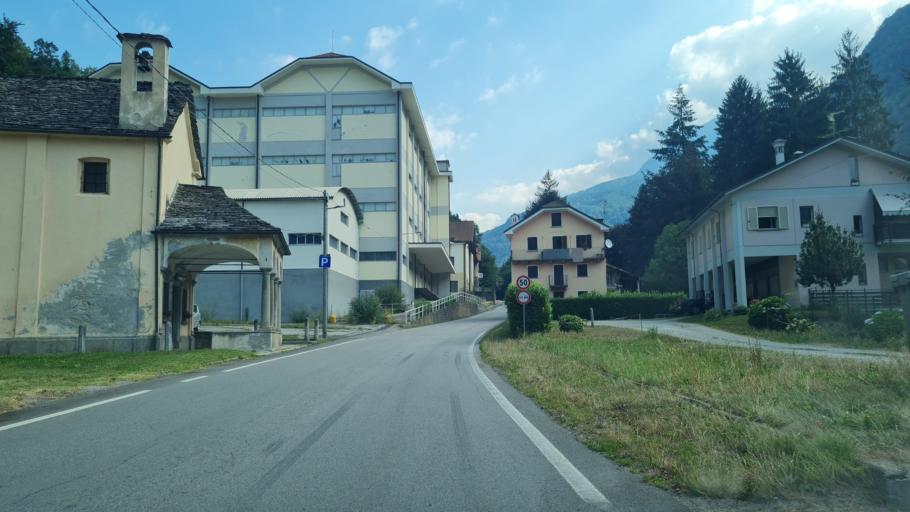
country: IT
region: Piedmont
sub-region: Provincia Verbano-Cusio-Ossola
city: Crodo
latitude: 46.2144
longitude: 8.3213
